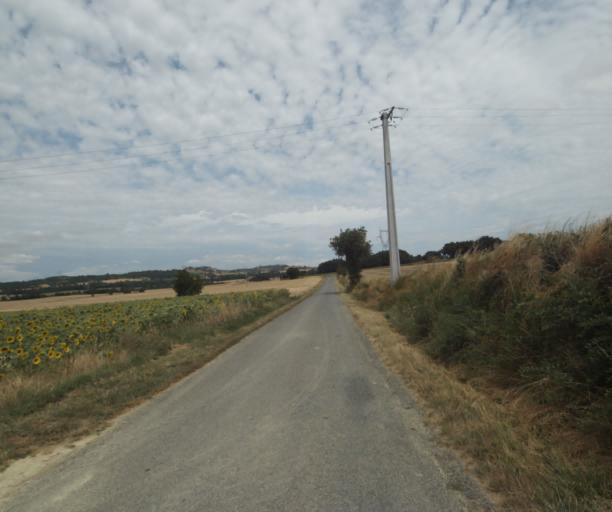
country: FR
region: Midi-Pyrenees
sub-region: Departement de la Haute-Garonne
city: Saint-Felix-Lauragais
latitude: 43.4122
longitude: 1.9041
